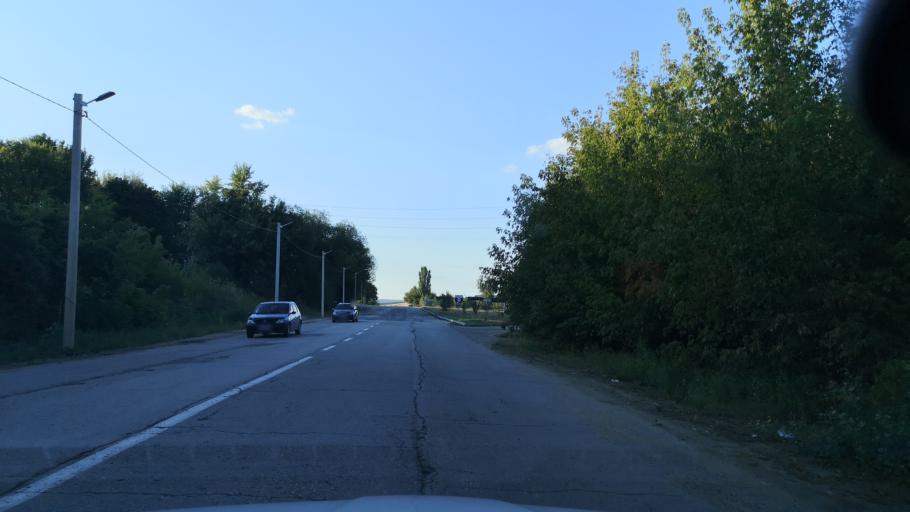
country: MD
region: Orhei
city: Orhei
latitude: 47.4012
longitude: 28.8189
